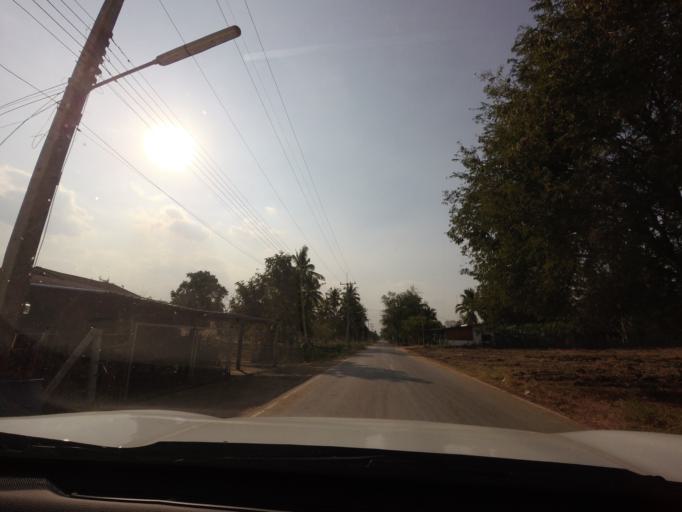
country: TH
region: Nakhon Ratchasima
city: Pak Chong
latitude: 14.6245
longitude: 101.4632
